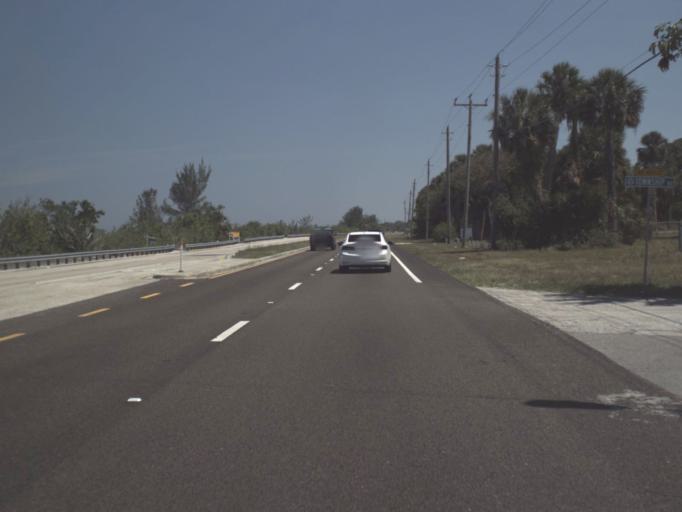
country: US
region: Florida
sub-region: Brevard County
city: Malabar
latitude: 27.9979
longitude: -80.5597
